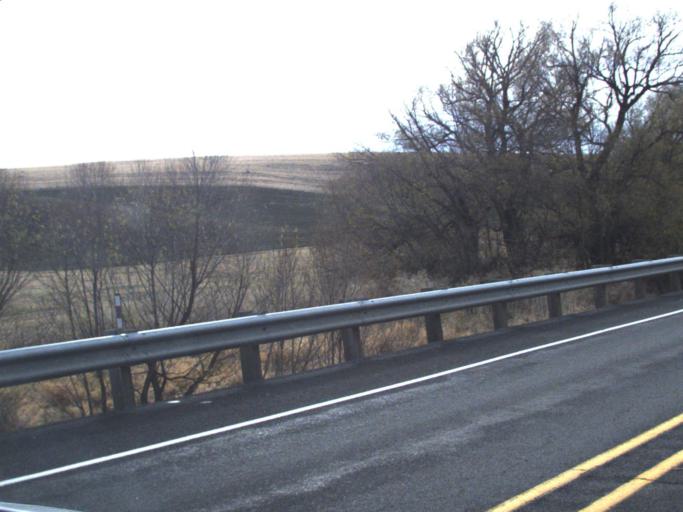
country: US
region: Washington
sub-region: Whitman County
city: Colfax
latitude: 46.8336
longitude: -117.4993
